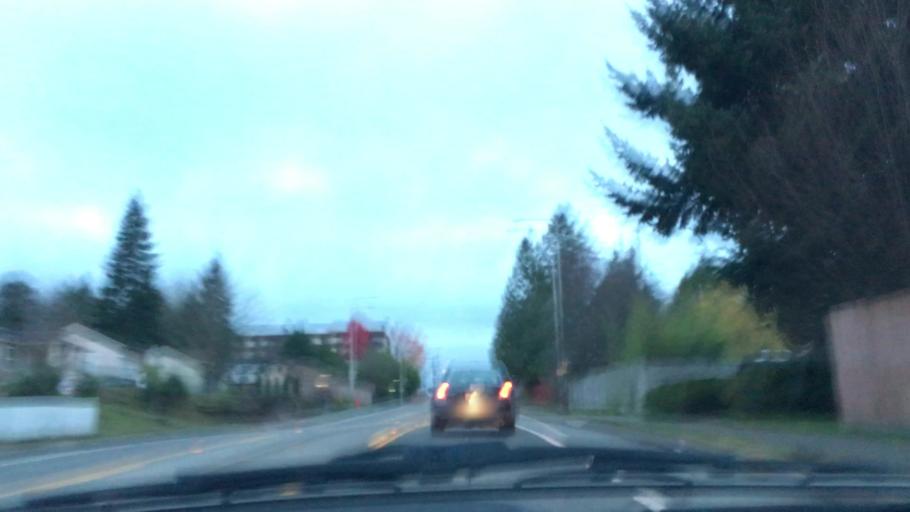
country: US
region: Washington
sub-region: King County
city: White Center
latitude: 47.5175
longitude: -122.3737
